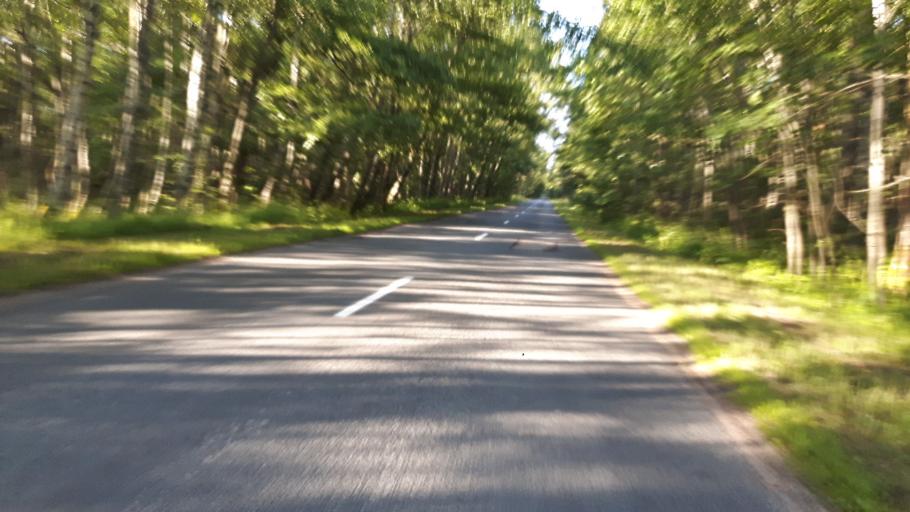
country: LT
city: Nida
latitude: 55.2271
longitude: 20.8977
